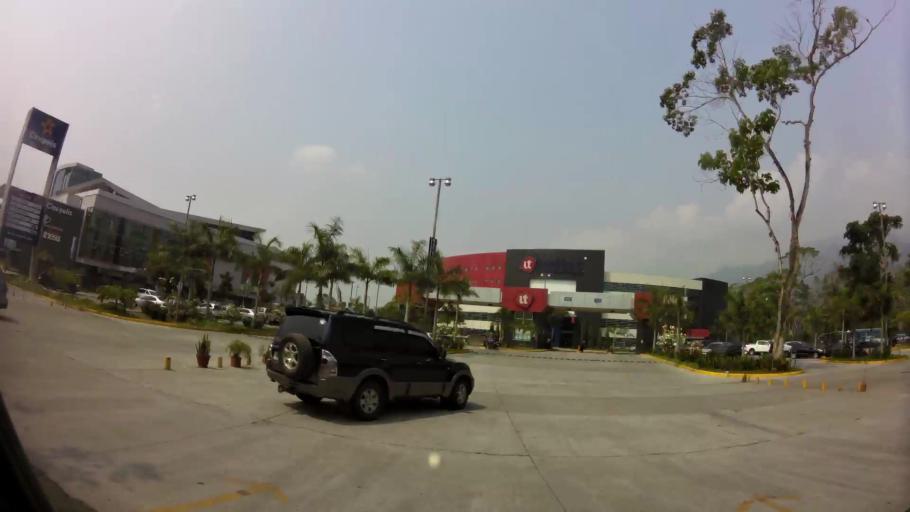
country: HN
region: Cortes
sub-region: San Pedro Sula
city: Pena Blanca
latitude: 15.5638
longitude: -88.0224
